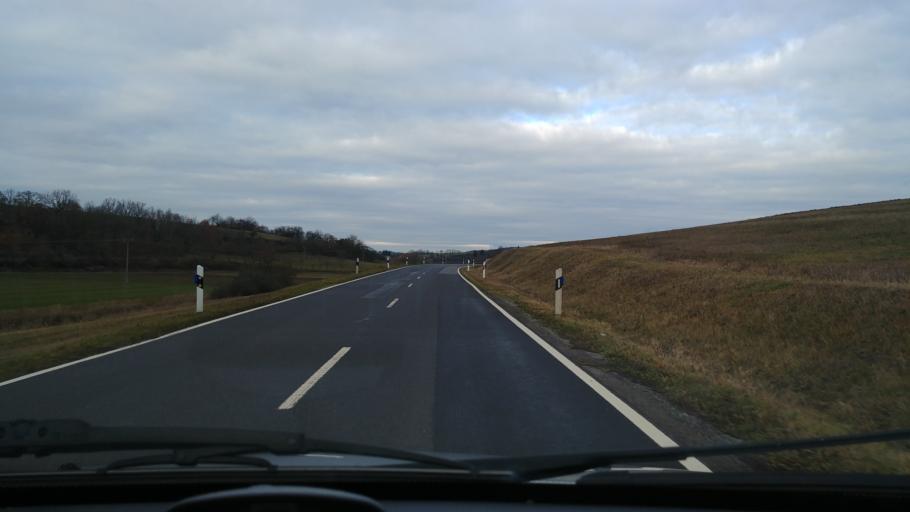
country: DE
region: Bavaria
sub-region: Regierungsbezirk Unterfranken
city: Arnstein
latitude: 50.0130
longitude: 9.9999
